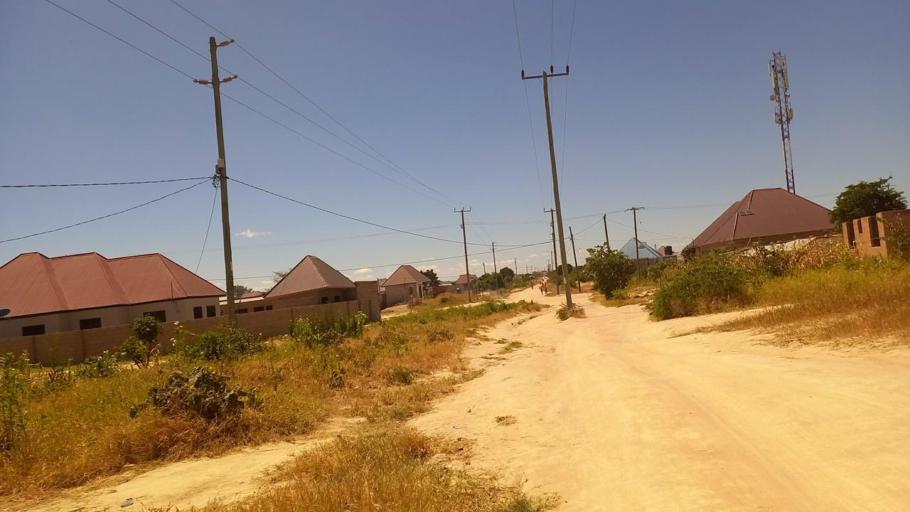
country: TZ
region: Dodoma
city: Dodoma
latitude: -6.1330
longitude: 35.7184
